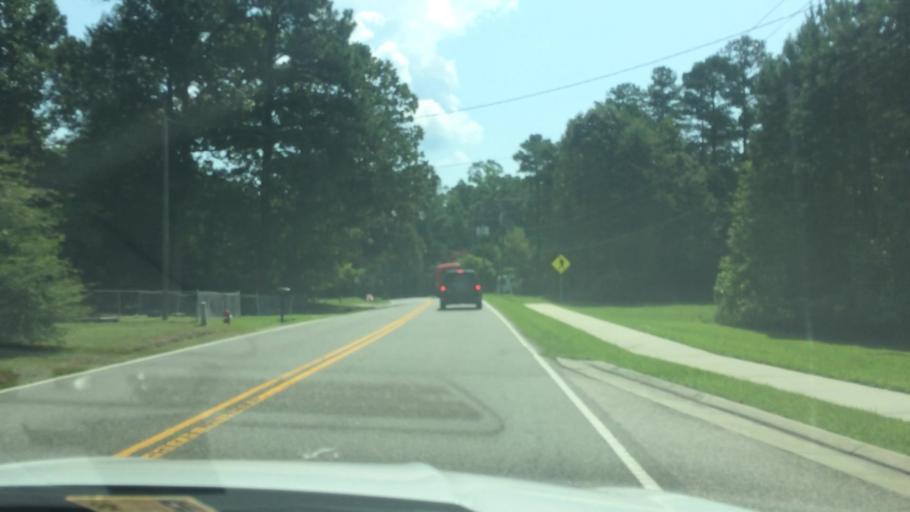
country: US
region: Virginia
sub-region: James City County
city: Williamsburg
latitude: 37.3162
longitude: -76.7823
